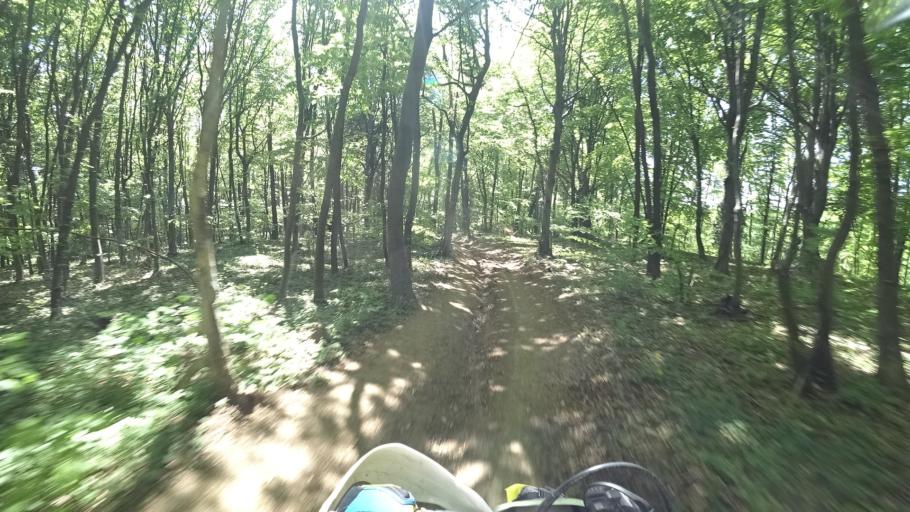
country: HR
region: Zagrebacka
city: Jablanovec
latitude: 45.8603
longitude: 15.8664
